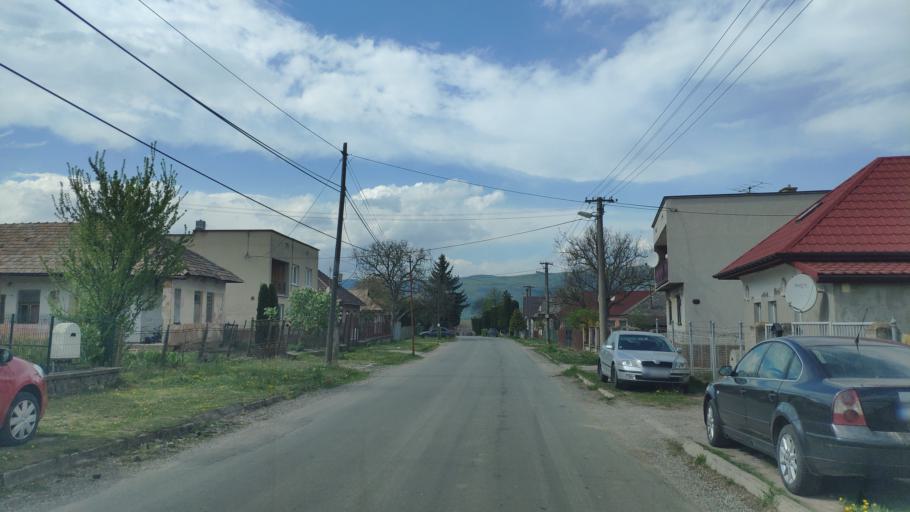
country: SK
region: Kosicky
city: Moldava nad Bodvou
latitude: 48.5829
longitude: 20.9222
